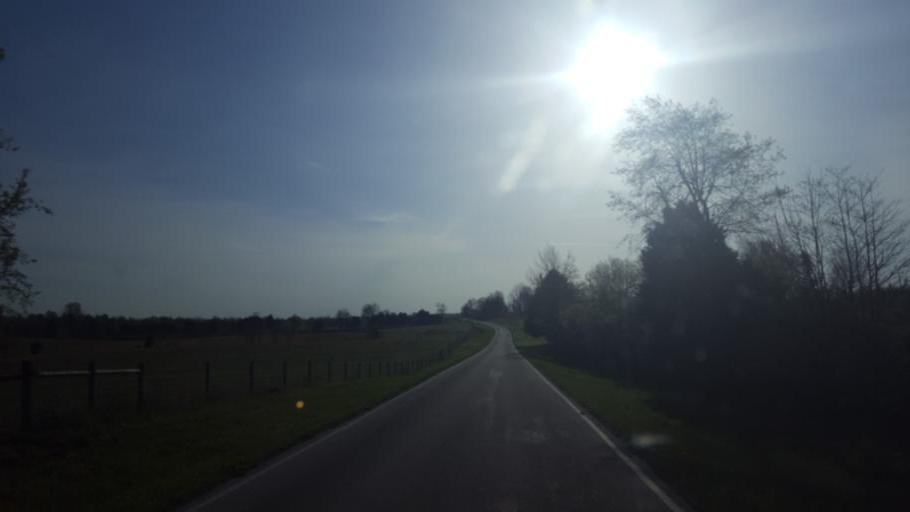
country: US
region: Kentucky
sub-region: Hart County
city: Munfordville
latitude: 37.4843
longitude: -85.9565
